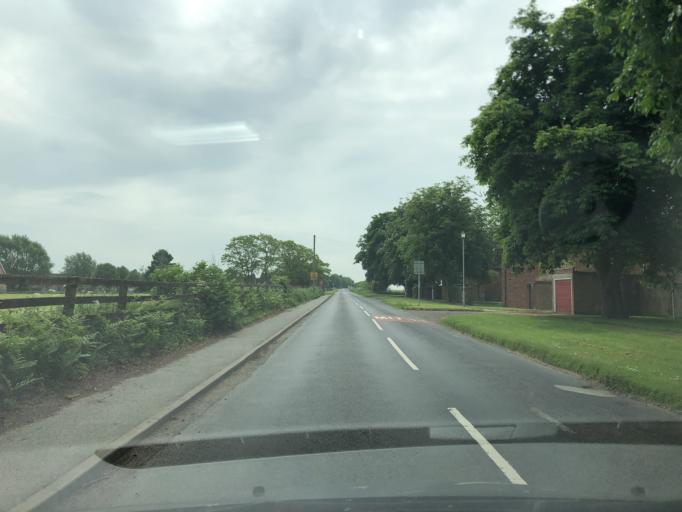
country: GB
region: England
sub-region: North Yorkshire
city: Boroughbridge
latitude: 54.1336
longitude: -1.4060
